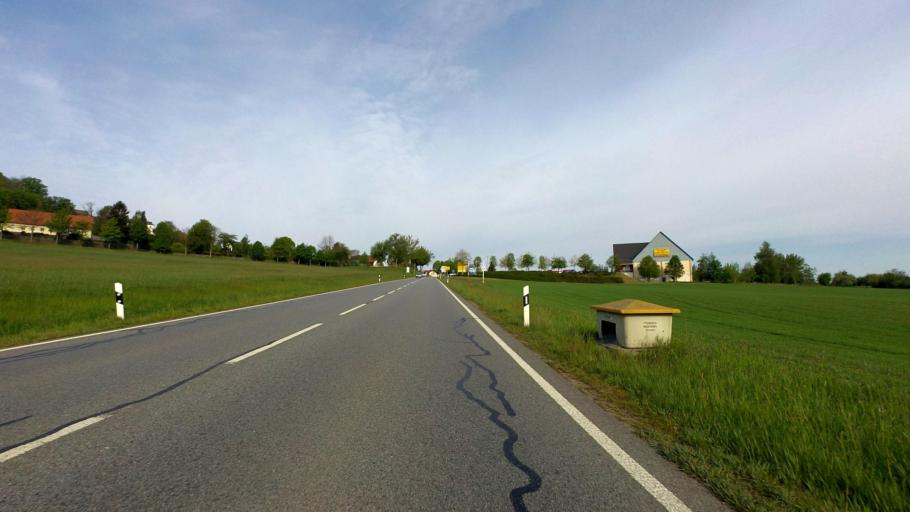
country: DE
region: Saxony
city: Stolpen
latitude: 51.0495
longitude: 14.0908
